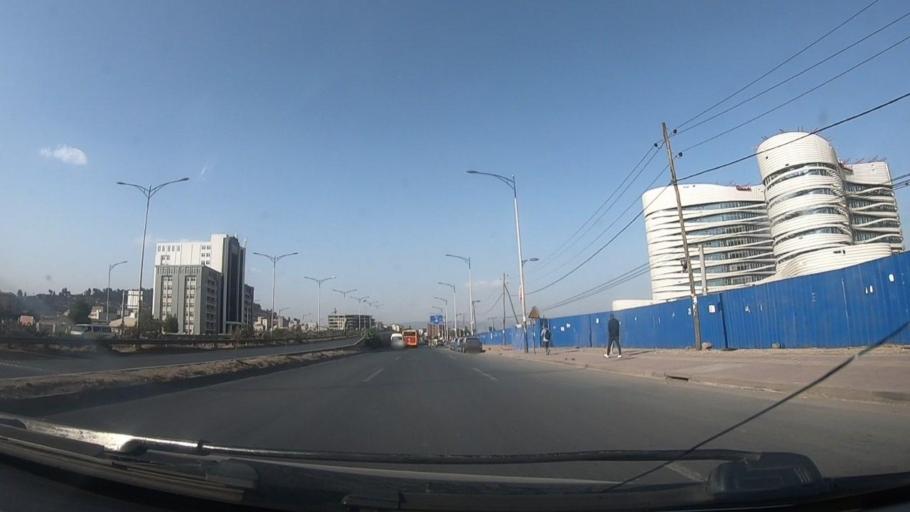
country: ET
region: Adis Abeba
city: Addis Ababa
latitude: 8.9341
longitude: 38.7345
